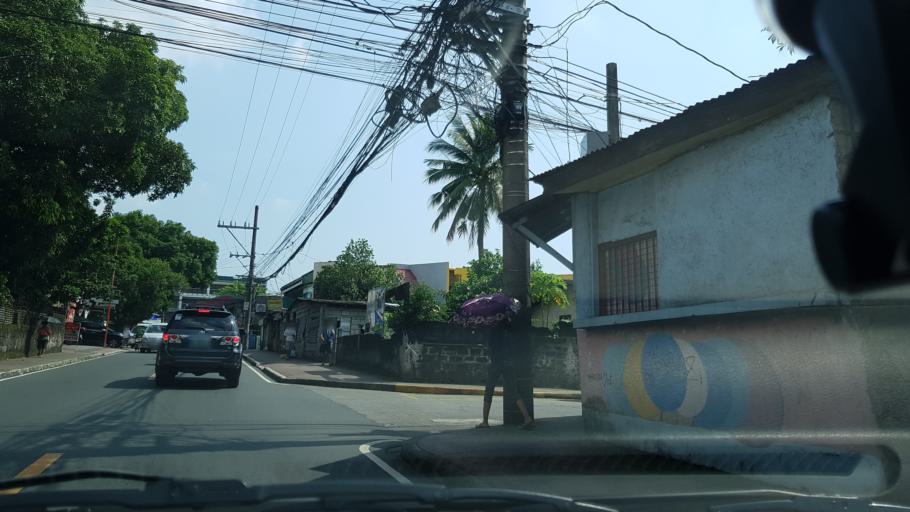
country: PH
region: Calabarzon
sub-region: Province of Rizal
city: San Mateo
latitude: 14.6623
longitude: 121.1123
